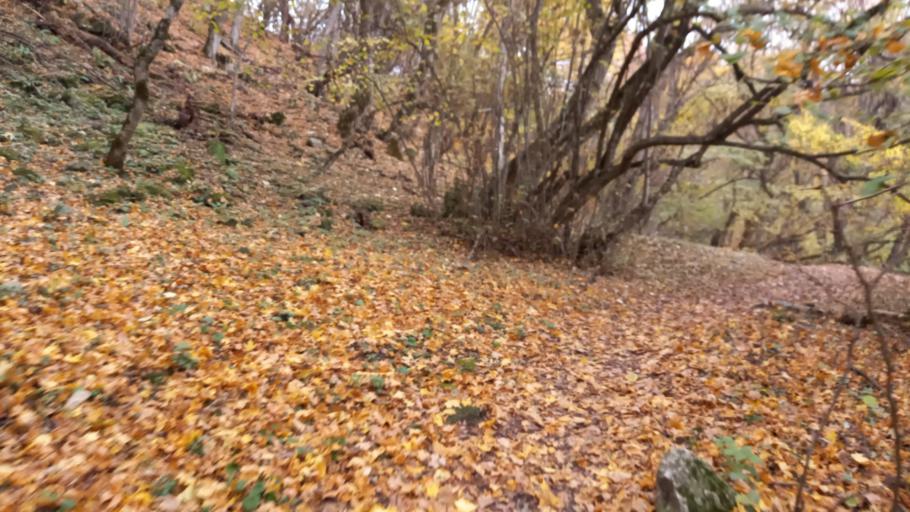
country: RU
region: Krasnodarskiy
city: Gubskaya
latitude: 44.2794
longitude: 40.5266
